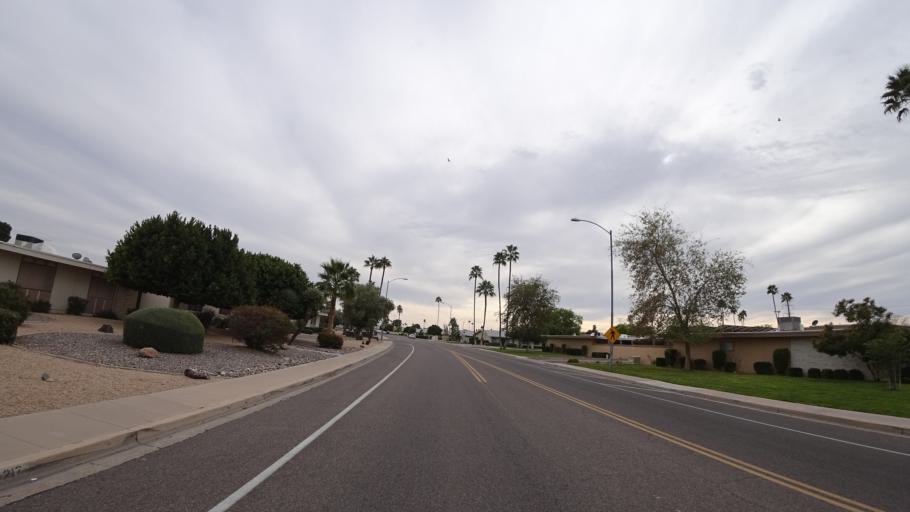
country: US
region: Arizona
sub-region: Maricopa County
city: Youngtown
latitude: 33.6130
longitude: -112.2997
